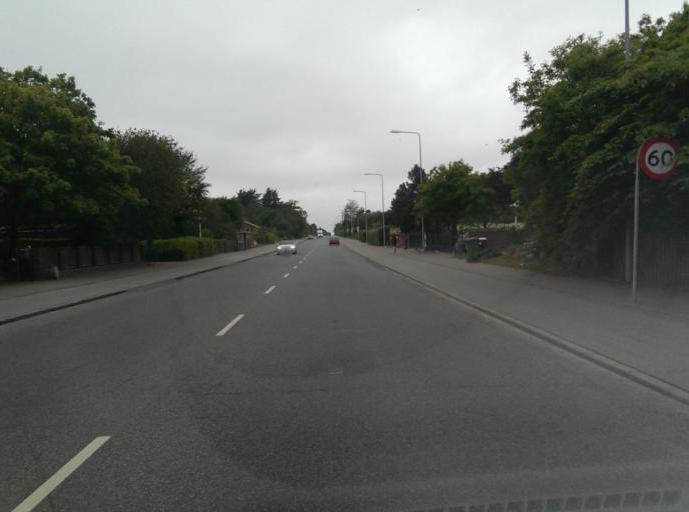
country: DK
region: South Denmark
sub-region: Fano Kommune
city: Nordby
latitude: 55.5132
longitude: 8.3760
